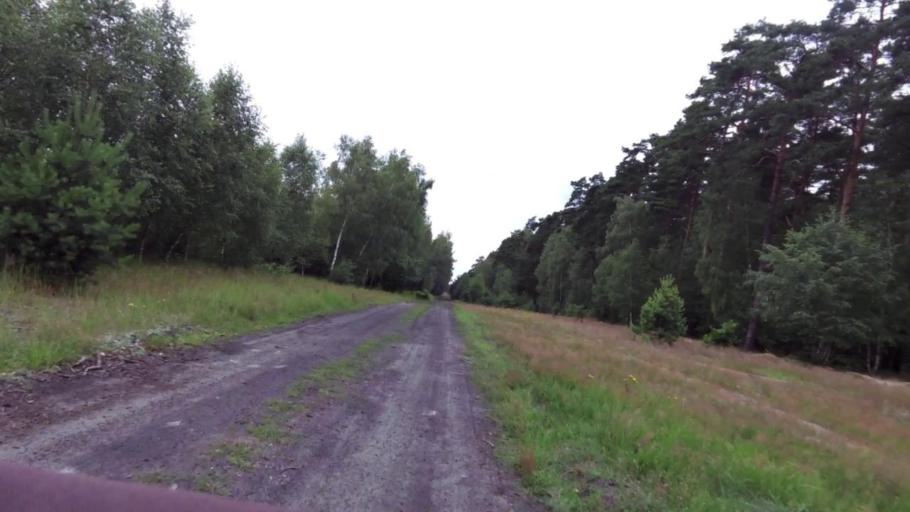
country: PL
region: West Pomeranian Voivodeship
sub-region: Powiat mysliborski
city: Debno
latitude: 52.8074
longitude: 14.6796
